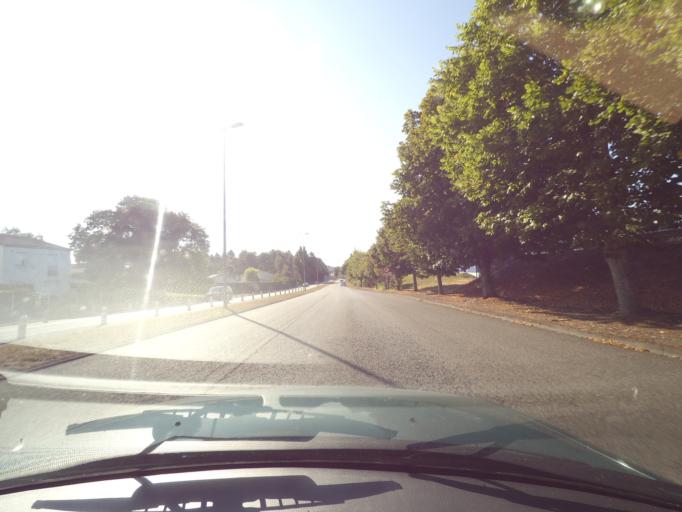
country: FR
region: Poitou-Charentes
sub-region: Departement des Deux-Sevres
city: Chatillon-sur-Thouet
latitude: 46.6523
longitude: -0.2284
